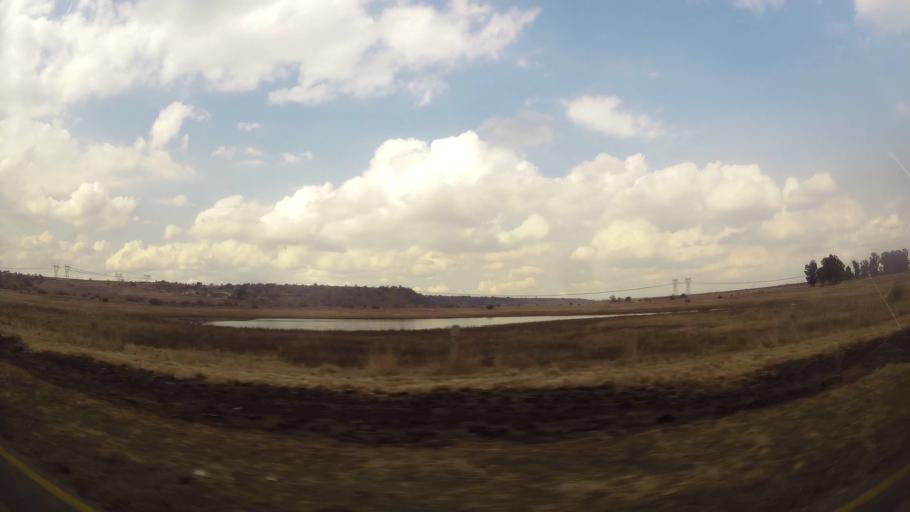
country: ZA
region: Orange Free State
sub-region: Fezile Dabi District Municipality
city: Sasolburg
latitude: -26.8091
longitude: 27.9112
